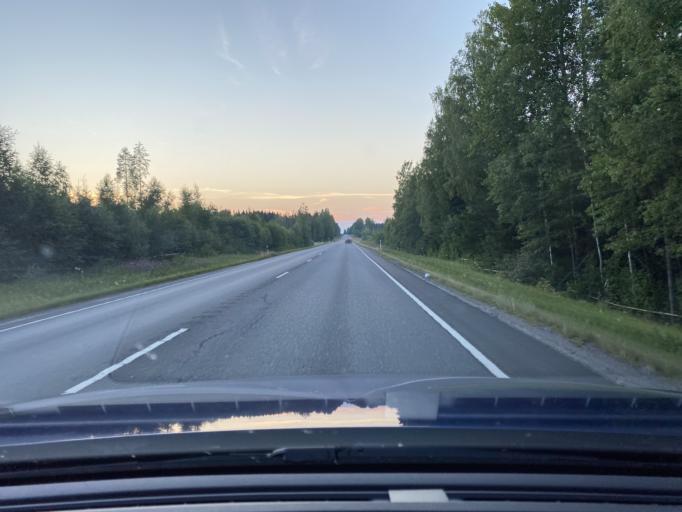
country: FI
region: Pirkanmaa
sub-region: Luoteis-Pirkanmaa
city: Ikaalinen
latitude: 61.8275
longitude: 22.9448
